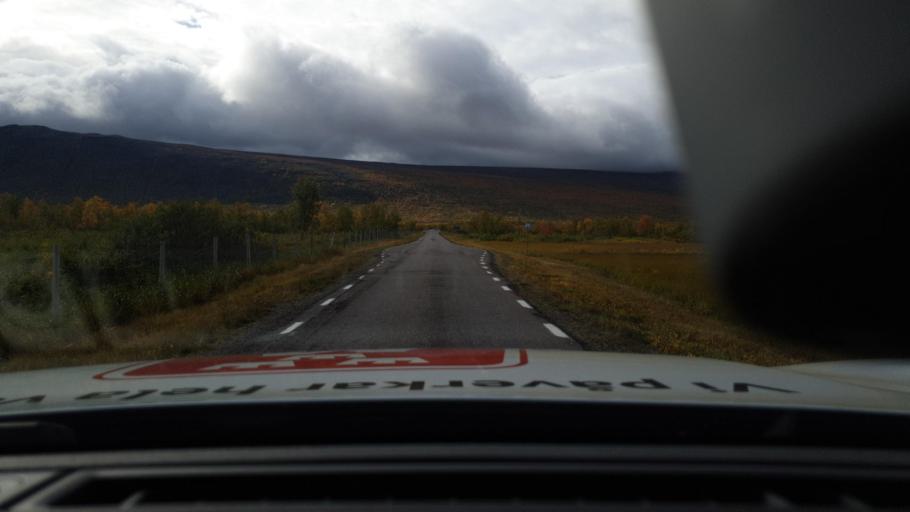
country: SE
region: Norrbotten
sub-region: Kiruna Kommun
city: Kiruna
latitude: 67.8587
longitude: 19.0255
